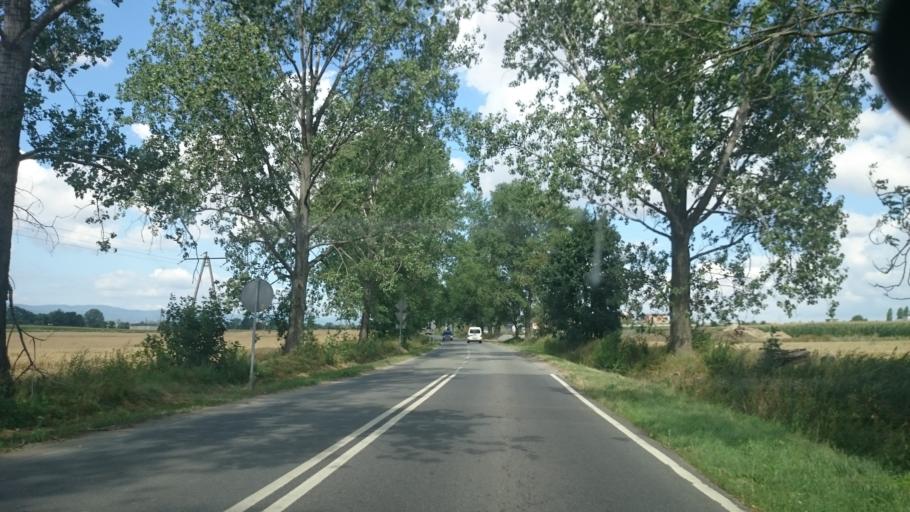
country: PL
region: Lower Silesian Voivodeship
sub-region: Powiat zabkowicki
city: Zabkowice Slaskie
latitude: 50.5766
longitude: 16.8373
